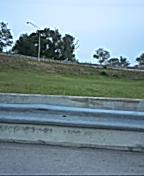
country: US
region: Kentucky
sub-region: Jefferson County
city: Hurstbourne Acres
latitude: 38.2229
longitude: -85.5788
